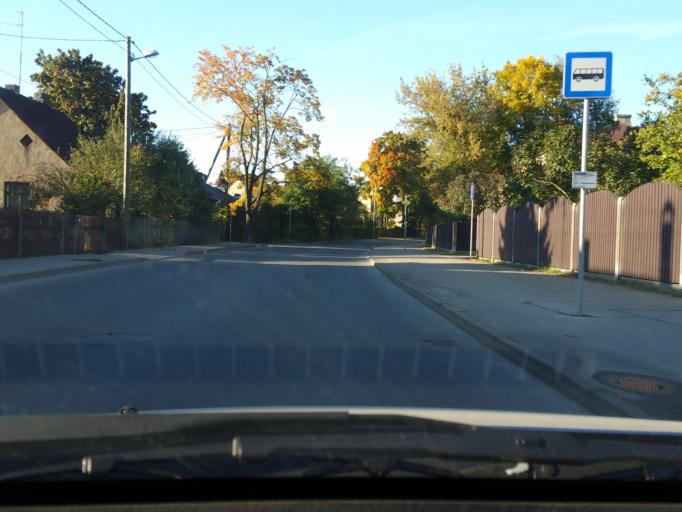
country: LV
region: Riga
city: Jaunciems
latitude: 56.9777
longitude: 24.1934
